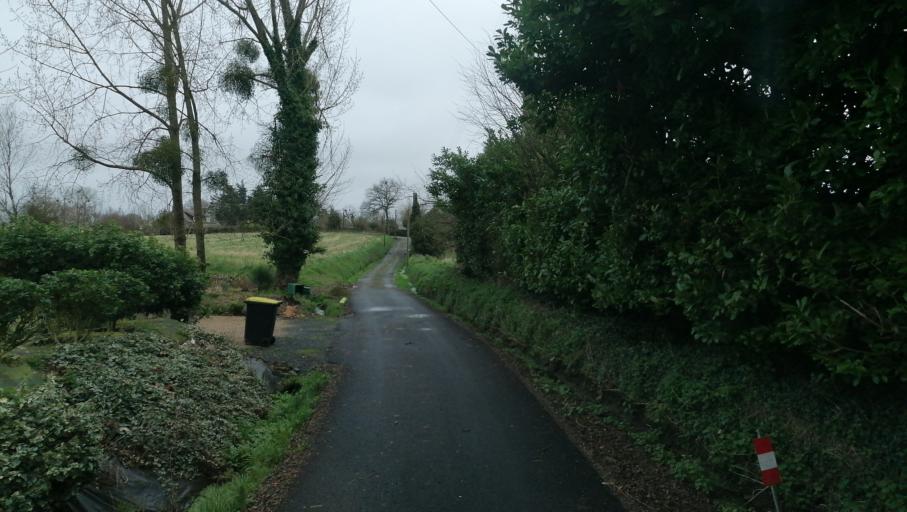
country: FR
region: Brittany
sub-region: Departement des Cotes-d'Armor
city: Saint-Agathon
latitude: 48.5816
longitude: -3.0730
